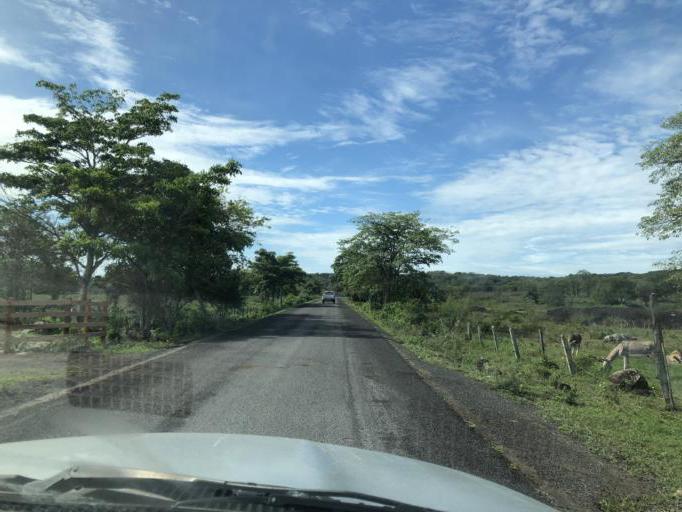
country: MX
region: Veracruz
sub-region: Alto Lucero de Gutierrez Barrios
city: Palma Sola
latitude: 19.7868
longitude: -96.5528
